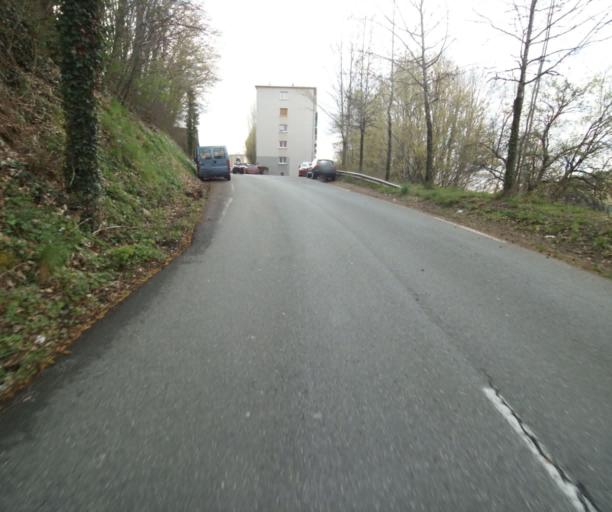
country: FR
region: Limousin
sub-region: Departement de la Correze
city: Tulle
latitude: 45.2538
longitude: 1.7595
